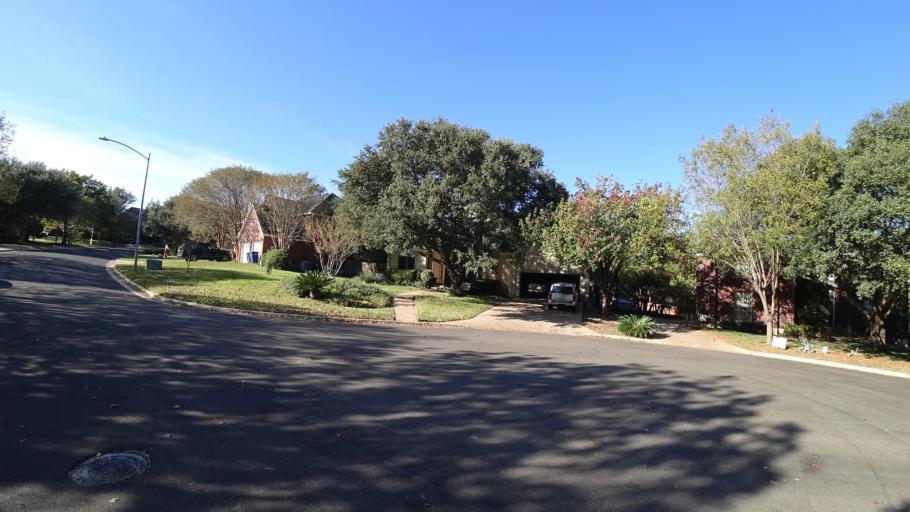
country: US
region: Texas
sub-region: Williamson County
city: Jollyville
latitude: 30.4178
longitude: -97.7768
